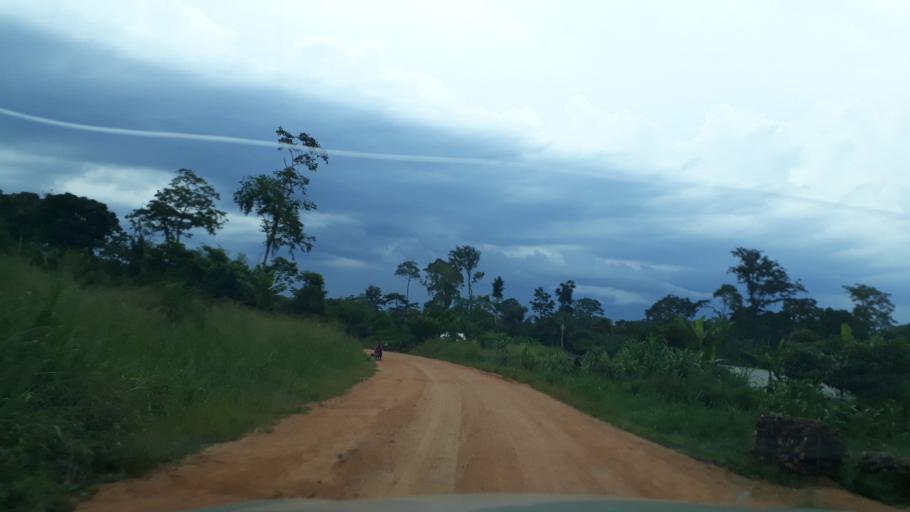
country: CD
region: Eastern Province
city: Bunia
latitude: 1.3546
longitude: 29.4733
